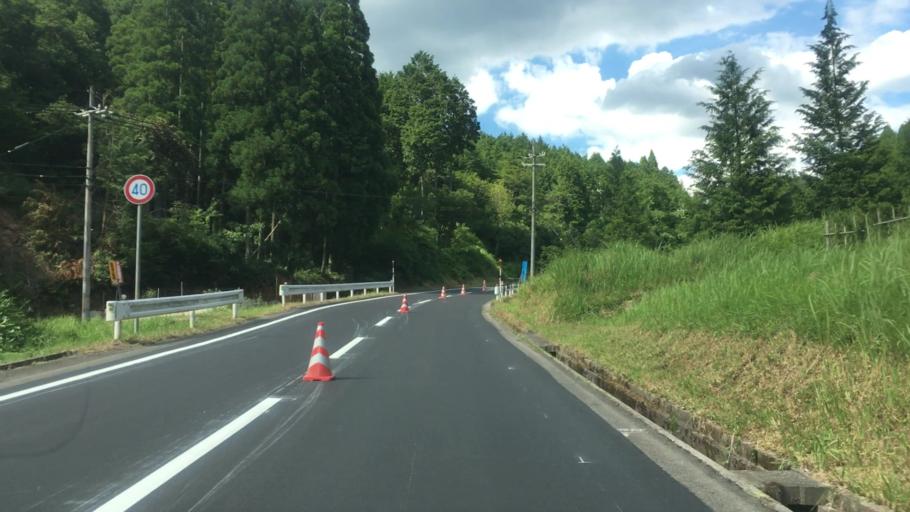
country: JP
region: Hyogo
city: Toyooka
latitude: 35.5064
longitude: 134.7774
